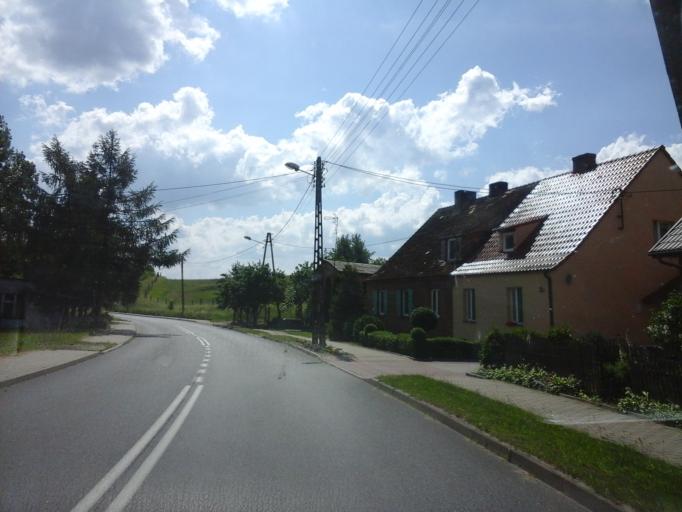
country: PL
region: West Pomeranian Voivodeship
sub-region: Powiat choszczenski
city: Bierzwnik
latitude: 53.1052
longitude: 15.6227
